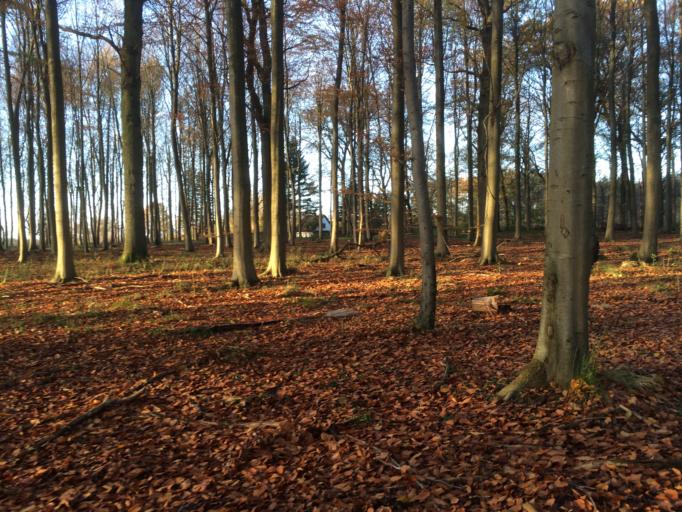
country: DK
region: Capital Region
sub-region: Fureso Kommune
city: Farum
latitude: 55.7935
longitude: 12.3470
